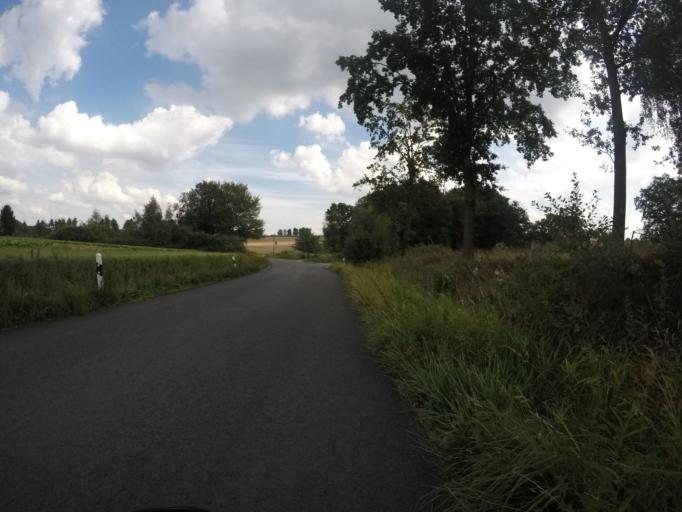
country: DE
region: North Rhine-Westphalia
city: Enger
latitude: 52.0979
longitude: 8.5930
